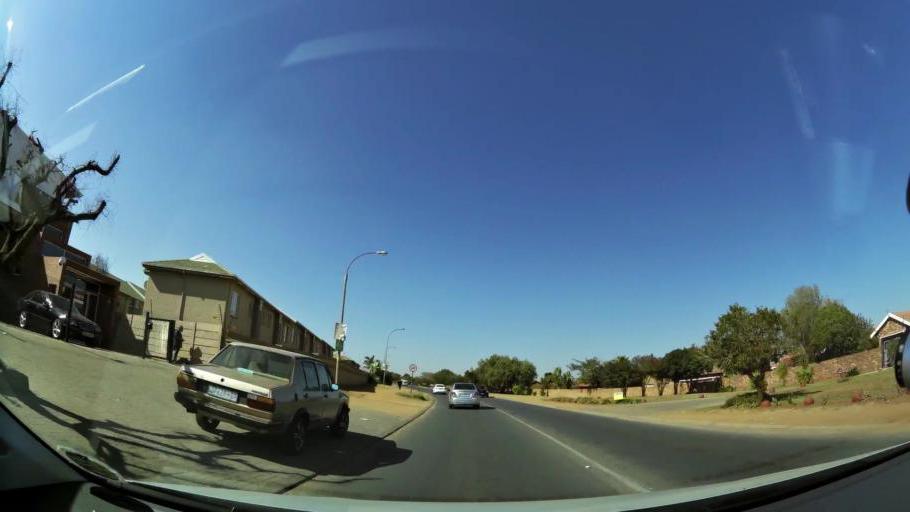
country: ZA
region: Gauteng
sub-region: City of Johannesburg Metropolitan Municipality
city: Modderfontein
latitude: -26.0626
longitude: 28.2166
